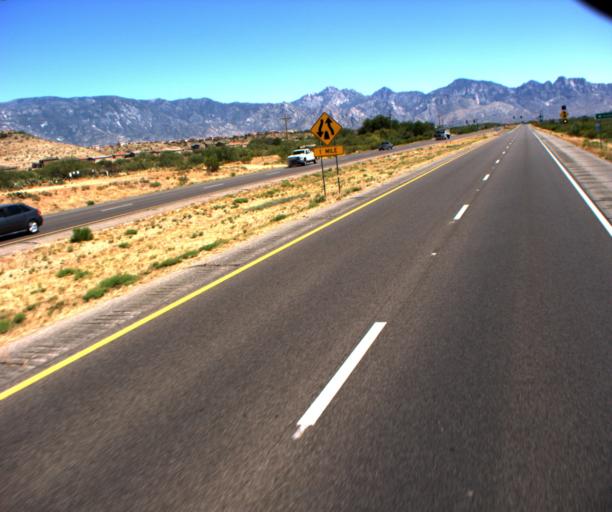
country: US
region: Arizona
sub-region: Pima County
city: Catalina
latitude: 32.5269
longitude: -110.9289
